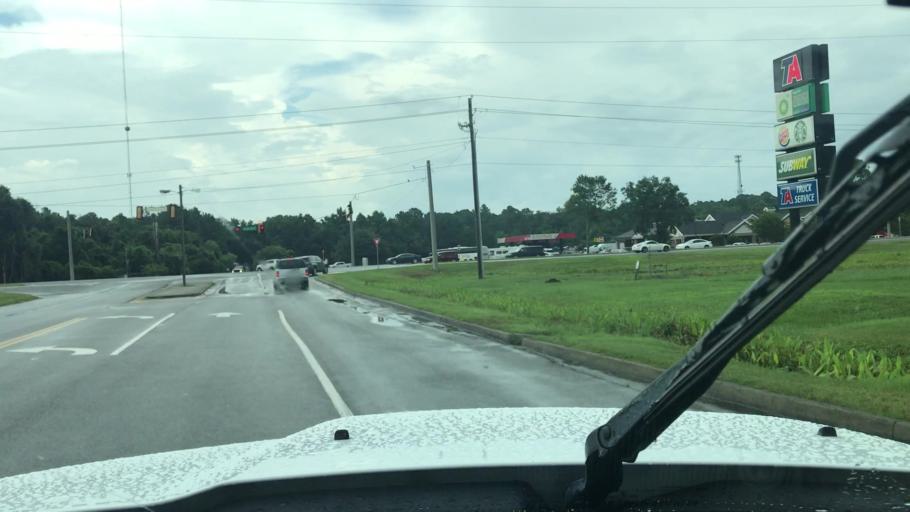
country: US
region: Georgia
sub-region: Glynn County
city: Brunswick
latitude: 31.1389
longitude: -81.5805
